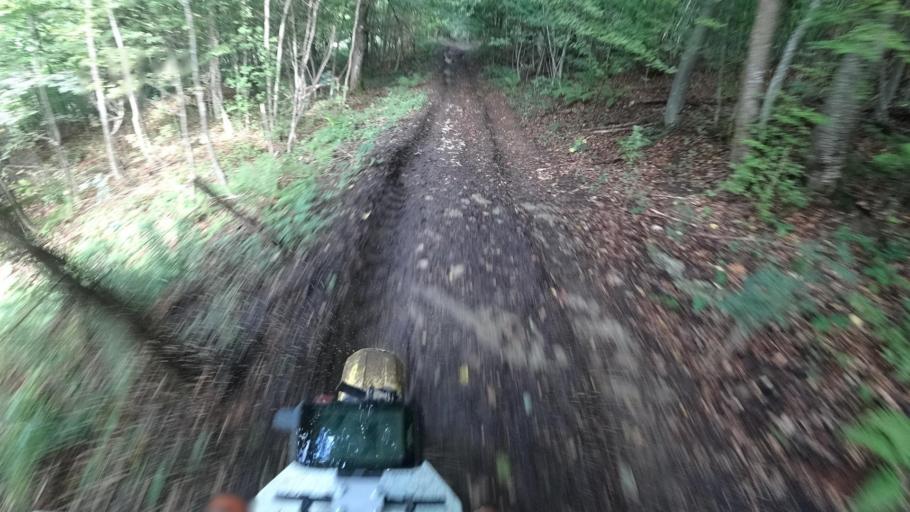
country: BA
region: Republika Srpska
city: Hiseti
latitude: 44.6654
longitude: 17.1693
